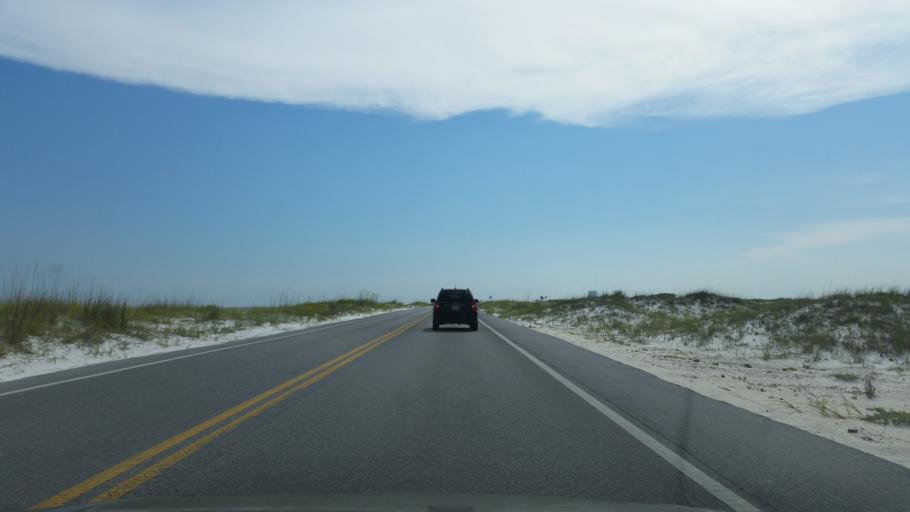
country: US
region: Florida
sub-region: Santa Rosa County
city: Tiger Point
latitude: 30.3524
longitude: -87.0311
